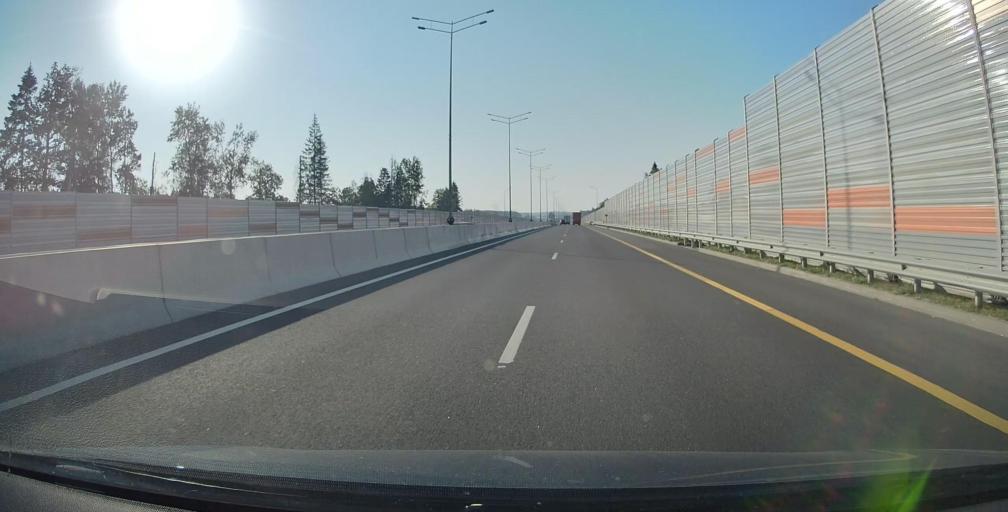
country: RU
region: Moskovskaya
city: Podosinki
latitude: 56.1705
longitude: 37.6665
